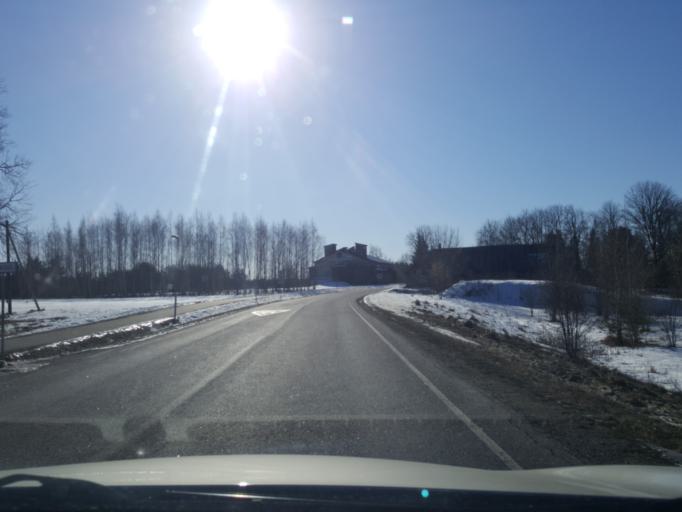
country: EE
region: Viljandimaa
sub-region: Viiratsi vald
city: Viiratsi
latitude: 58.4287
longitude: 25.6839
